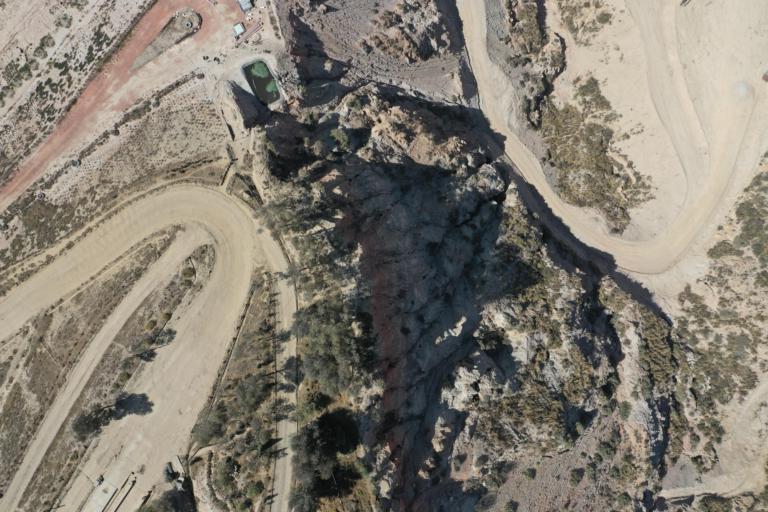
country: BO
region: La Paz
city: La Paz
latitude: -16.5538
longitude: -68.1284
